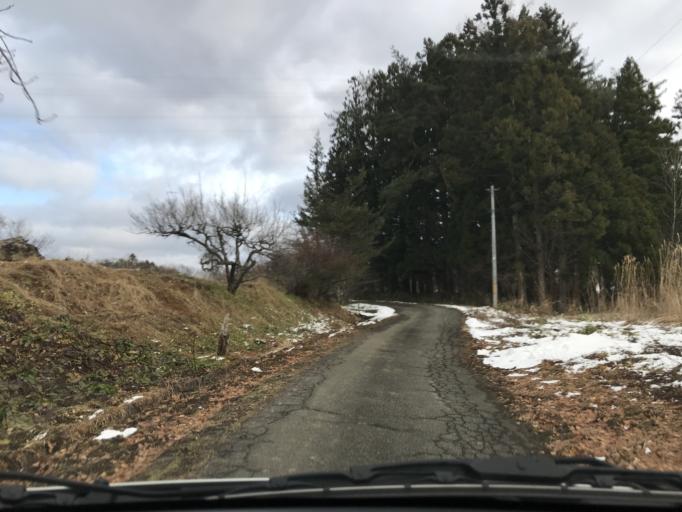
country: JP
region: Iwate
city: Ichinoseki
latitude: 38.9826
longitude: 141.0044
